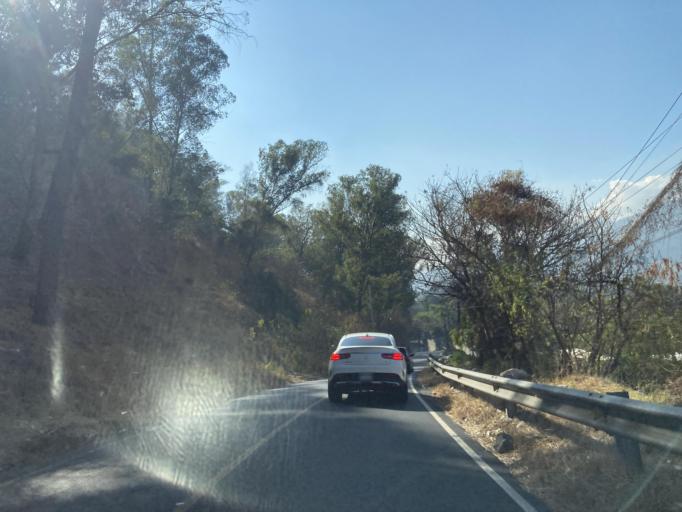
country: GT
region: Guatemala
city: Amatitlan
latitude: 14.4936
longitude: -90.6187
